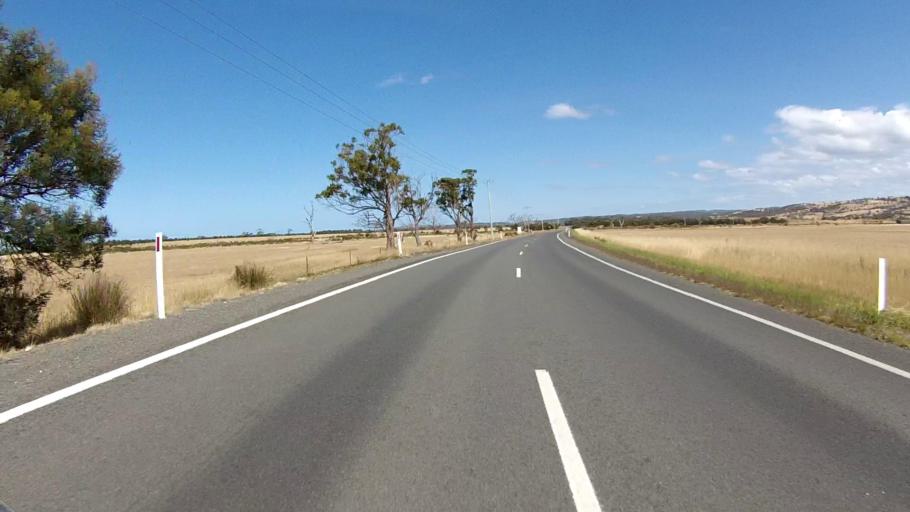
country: AU
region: Tasmania
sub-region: Break O'Day
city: St Helens
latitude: -42.0886
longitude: 148.0670
